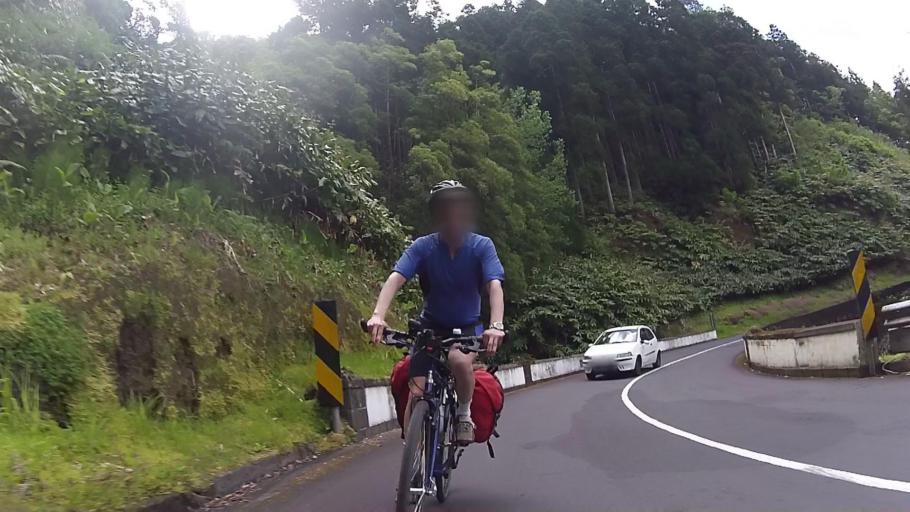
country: PT
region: Azores
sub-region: Povoacao
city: Furnas
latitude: 37.7670
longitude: -25.2882
